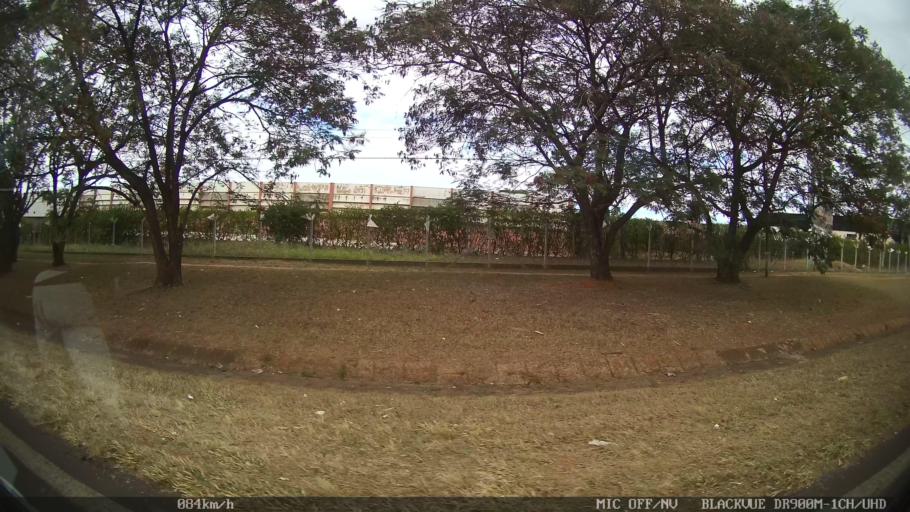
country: BR
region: Sao Paulo
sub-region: Sao Jose Do Rio Preto
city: Sao Jose do Rio Preto
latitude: -20.8118
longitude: -49.4872
